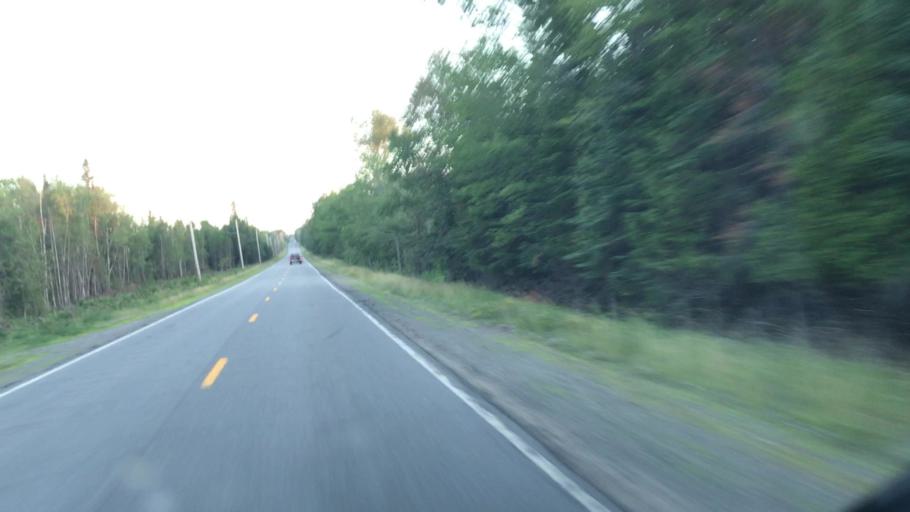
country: US
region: Maine
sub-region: Penobscot County
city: Medway
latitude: 45.6079
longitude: -68.3067
